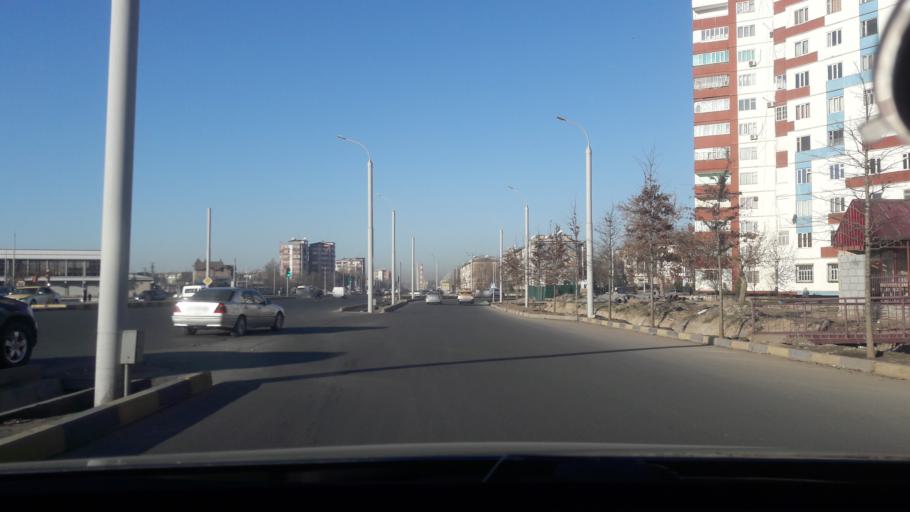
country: TJ
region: Dushanbe
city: Dushanbe
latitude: 38.5586
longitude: 68.7568
